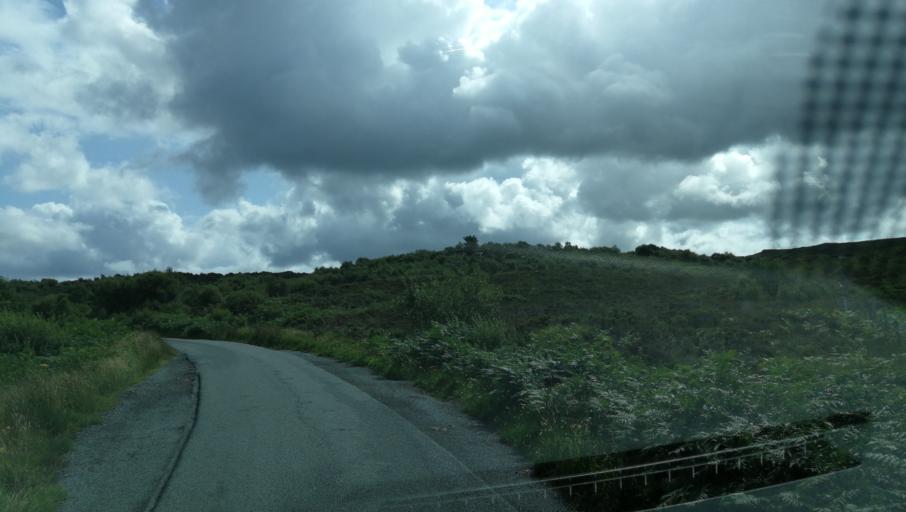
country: GB
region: Scotland
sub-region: Highland
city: Portree
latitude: 57.3840
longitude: -6.1852
